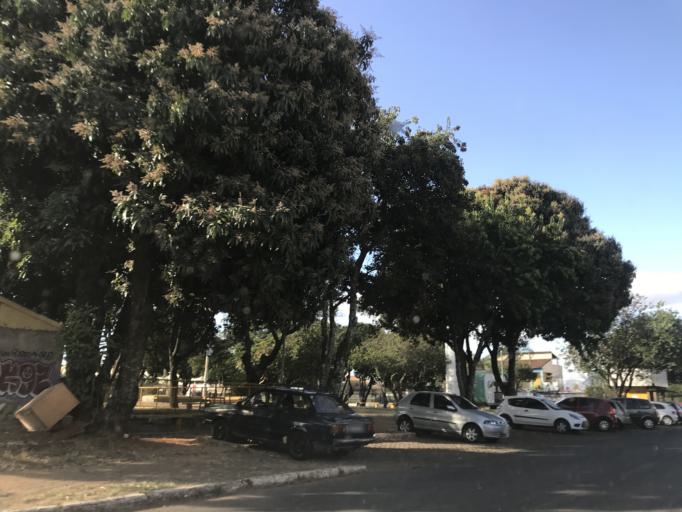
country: BR
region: Federal District
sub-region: Brasilia
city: Brasilia
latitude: -15.8157
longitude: -47.9886
